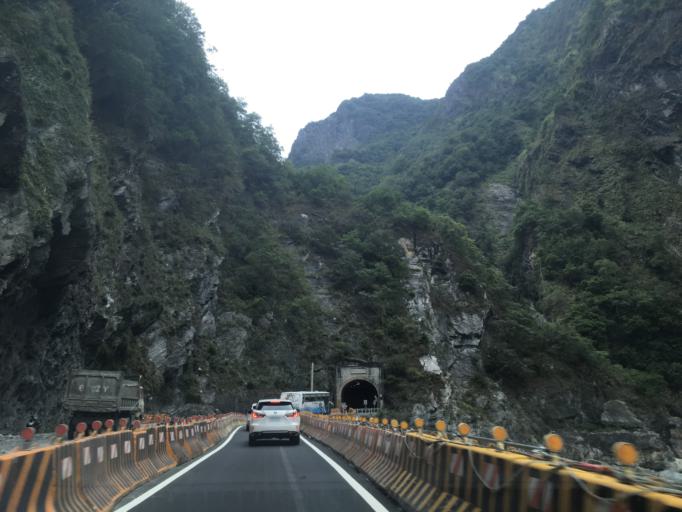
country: TW
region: Taiwan
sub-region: Hualien
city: Hualian
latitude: 24.1779
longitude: 121.4997
